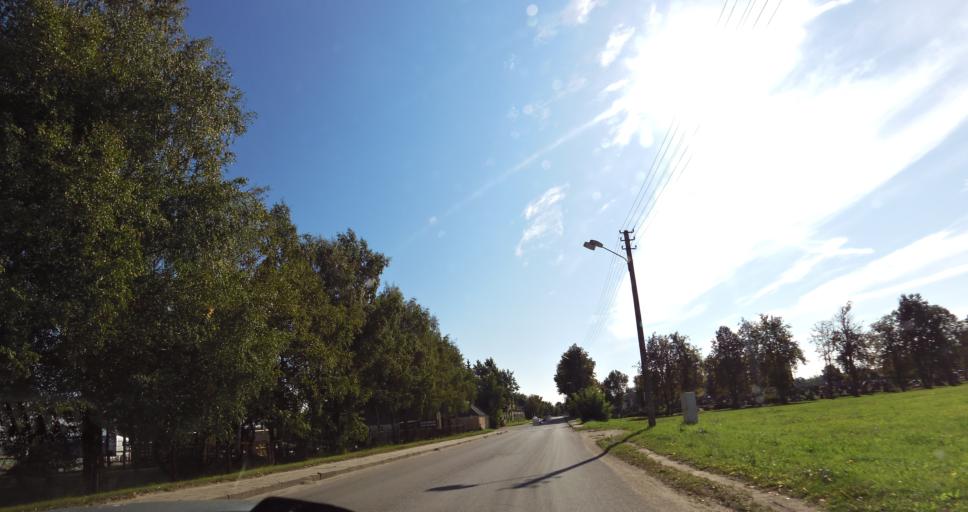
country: LT
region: Panevezys
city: Pasvalys
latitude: 56.0660
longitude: 24.3886
